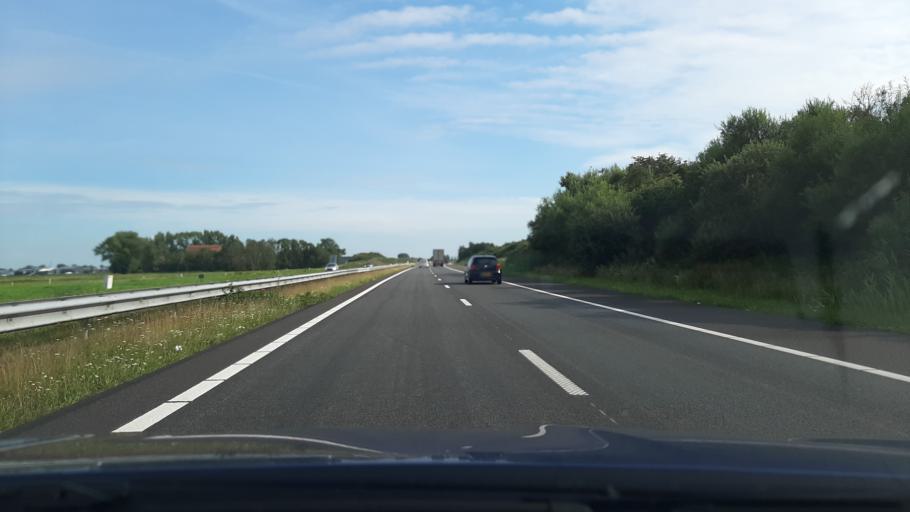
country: NL
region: Friesland
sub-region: Gemeente Boarnsterhim
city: Reduzum
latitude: 53.1100
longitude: 5.8140
